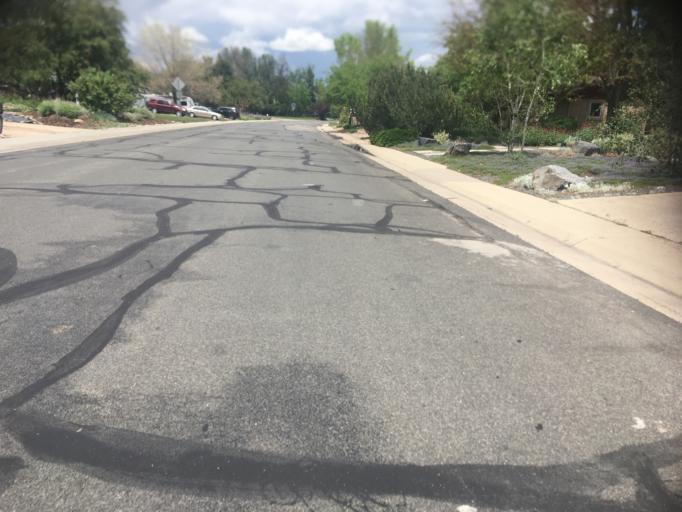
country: US
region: Colorado
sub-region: Boulder County
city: Boulder
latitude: 40.0032
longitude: -105.2309
